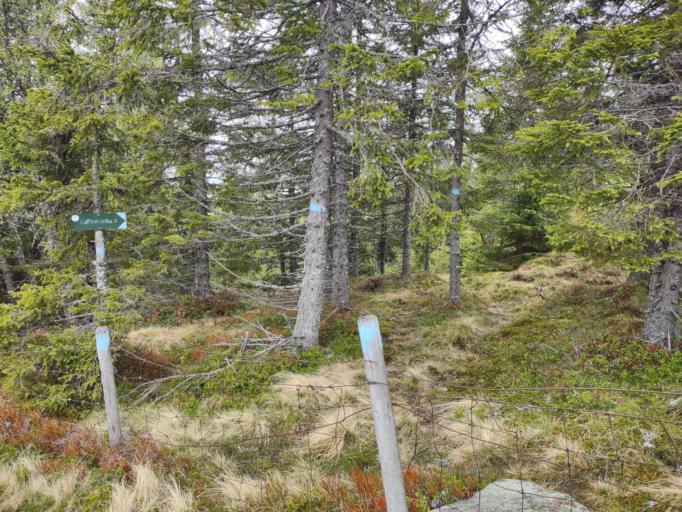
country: NO
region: Oppland
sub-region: Lunner
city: Grua
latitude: 60.3452
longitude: 10.7999
